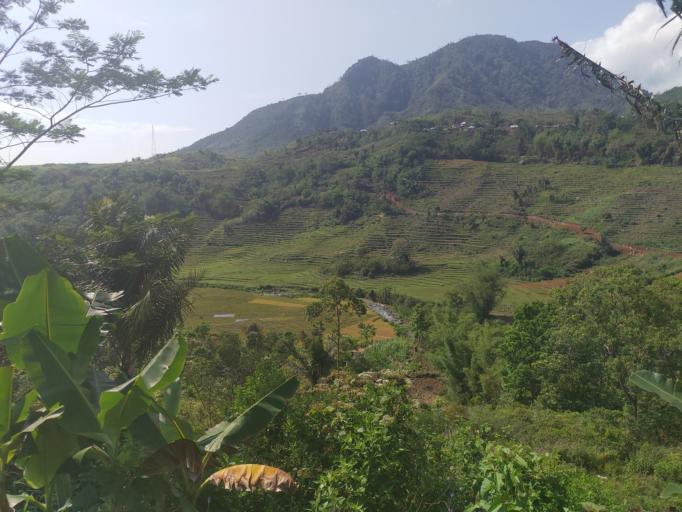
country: ID
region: East Nusa Tenggara
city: Pora
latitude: -8.6457
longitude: 120.3435
